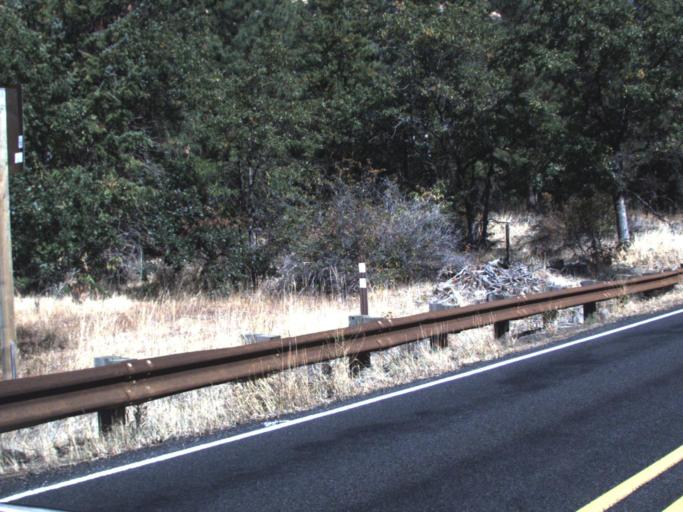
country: US
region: Washington
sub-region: Yakima County
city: Tieton
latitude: 46.7063
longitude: -120.8901
